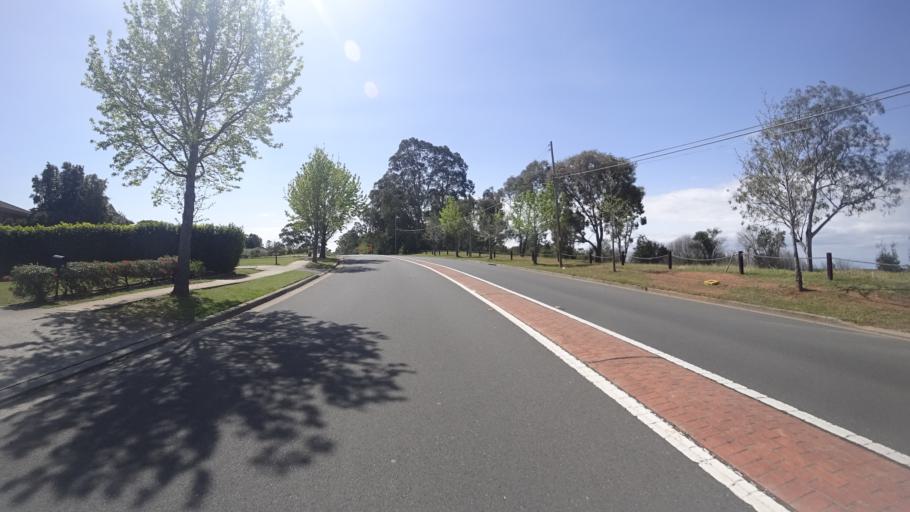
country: AU
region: New South Wales
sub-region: Campbelltown Municipality
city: Glenfield
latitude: -33.9570
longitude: 150.9060
